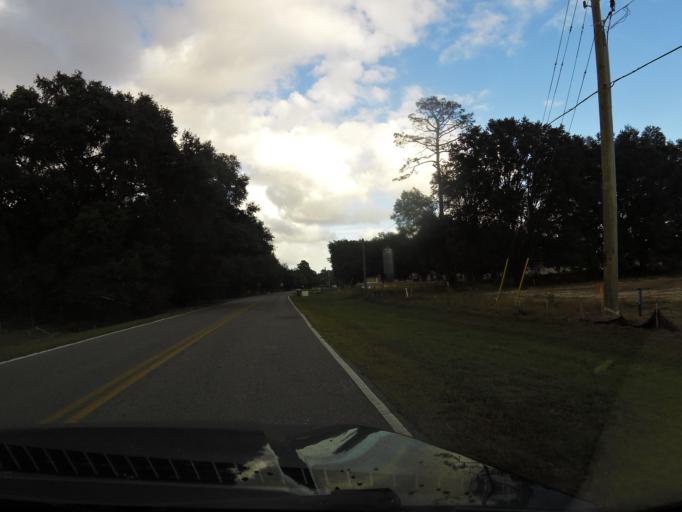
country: US
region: Florida
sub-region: Clay County
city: Asbury Lake
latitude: 30.0475
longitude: -81.7733
